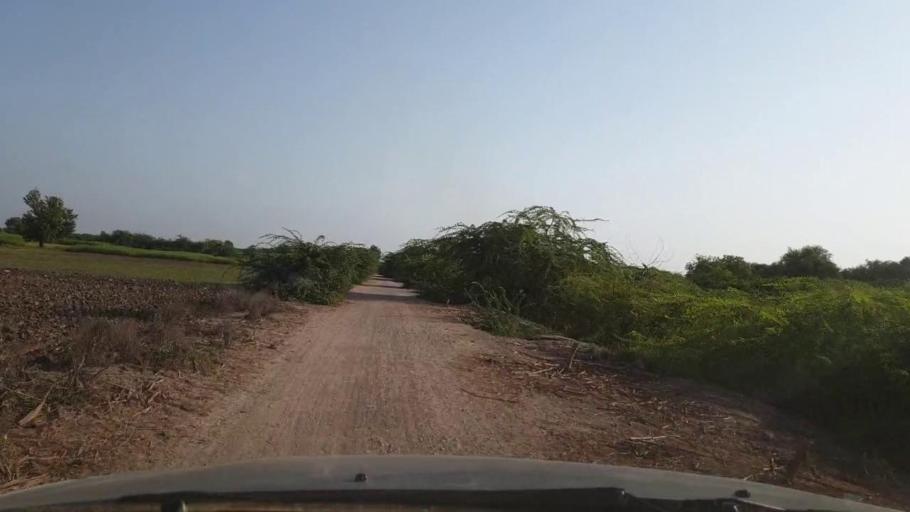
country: PK
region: Sindh
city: Tando Ghulam Ali
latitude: 25.1200
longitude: 68.9407
